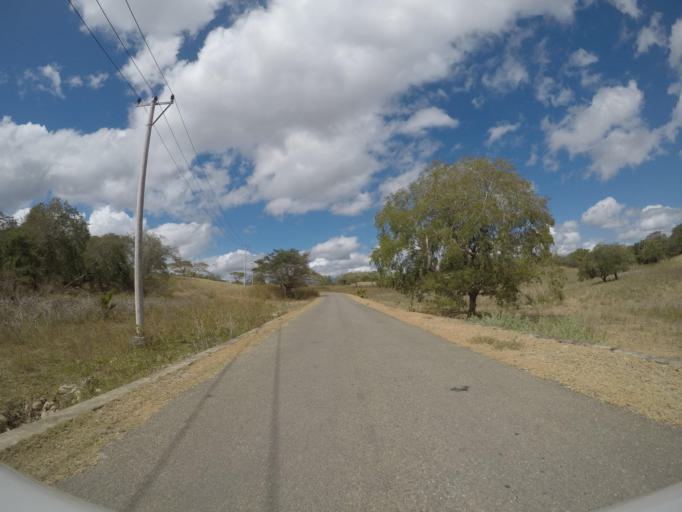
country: TL
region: Lautem
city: Lospalos
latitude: -8.4295
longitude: 126.8306
